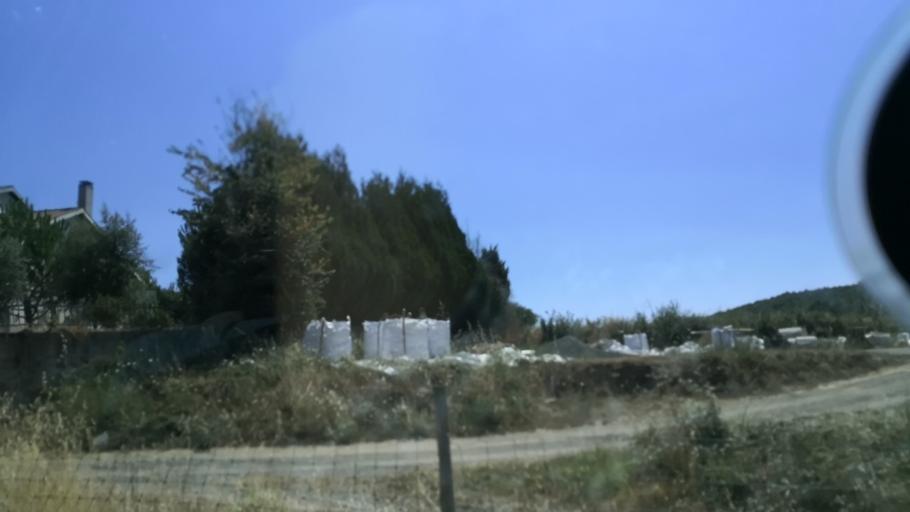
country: PT
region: Braganca
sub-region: Braganca Municipality
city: Braganca
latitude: 41.7708
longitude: -6.7915
